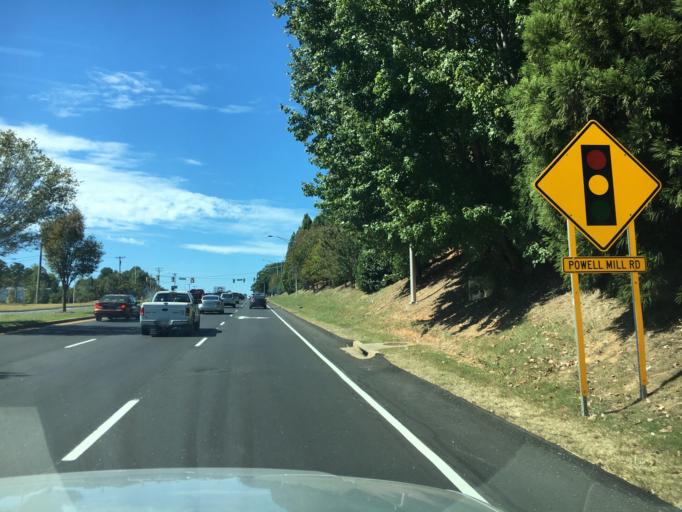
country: US
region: South Carolina
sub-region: Spartanburg County
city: Saxon
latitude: 34.9382
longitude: -81.9737
